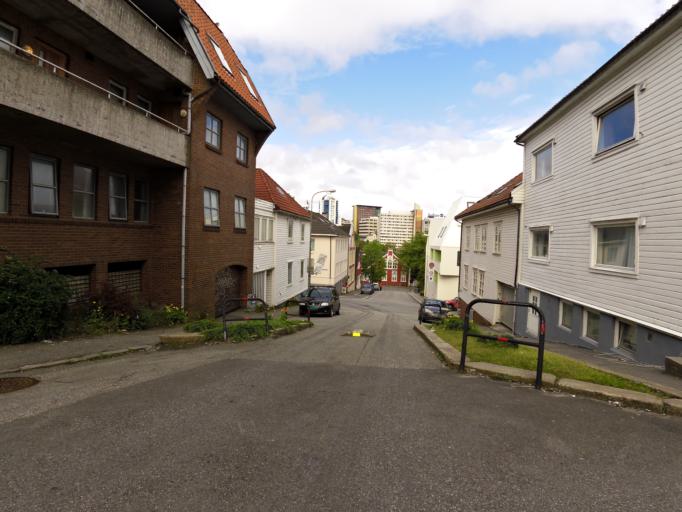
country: NO
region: Rogaland
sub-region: Stavanger
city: Stavanger
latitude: 58.9673
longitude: 5.7363
